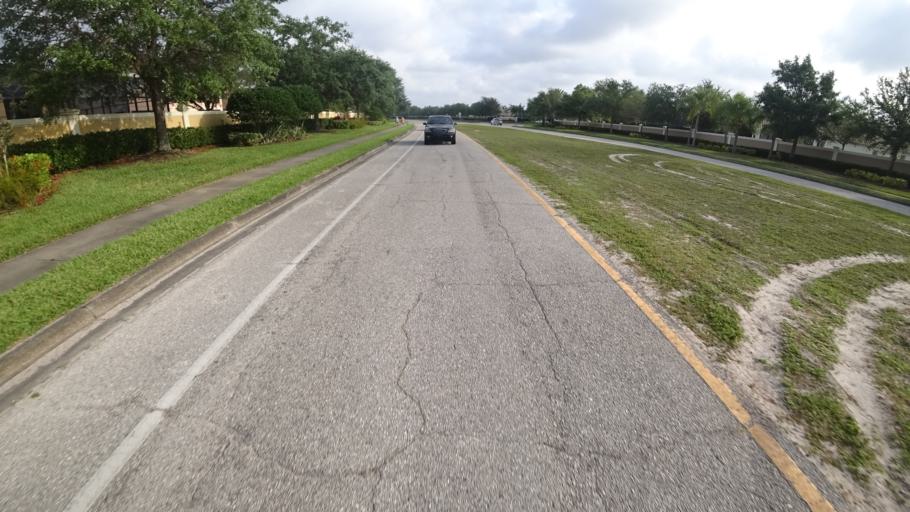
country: US
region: Florida
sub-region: Sarasota County
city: North Sarasota
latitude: 27.4221
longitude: -82.5127
